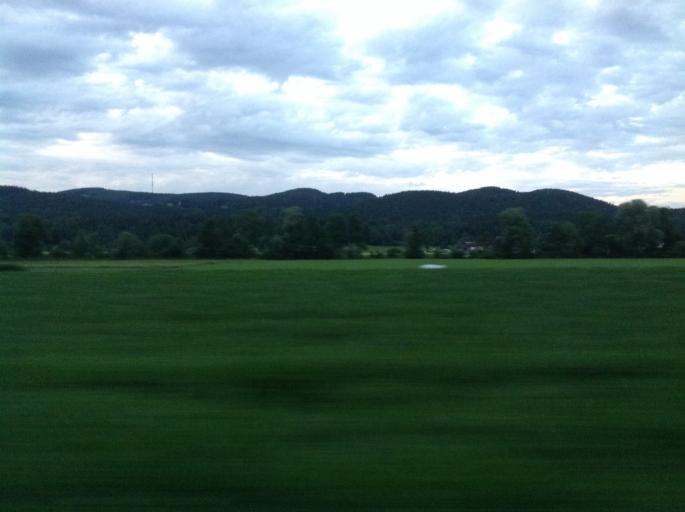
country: DE
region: Bavaria
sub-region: Upper Bavaria
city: Piding
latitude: 47.7682
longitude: 12.8991
